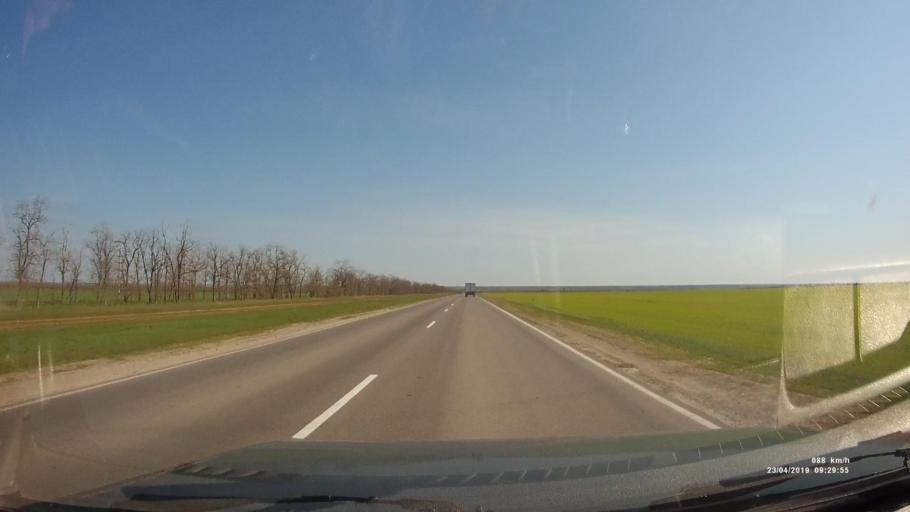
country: RU
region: Rostov
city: Gundorovskiy
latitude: 46.7658
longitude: 41.8103
